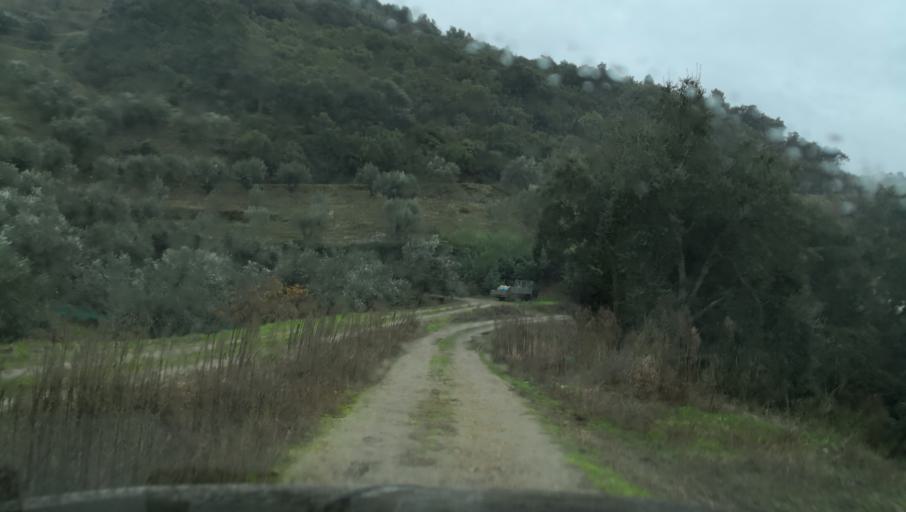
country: PT
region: Vila Real
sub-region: Vila Real
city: Vila Real
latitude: 41.2507
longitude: -7.7476
